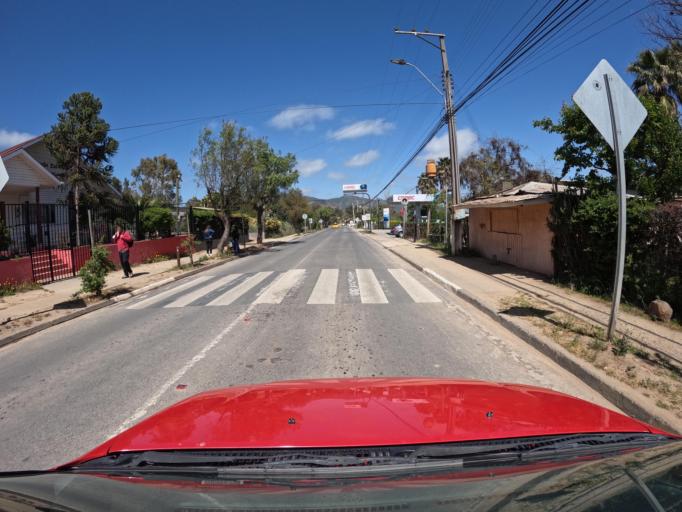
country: CL
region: O'Higgins
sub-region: Provincia de Colchagua
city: Santa Cruz
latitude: -34.7248
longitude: -71.6410
